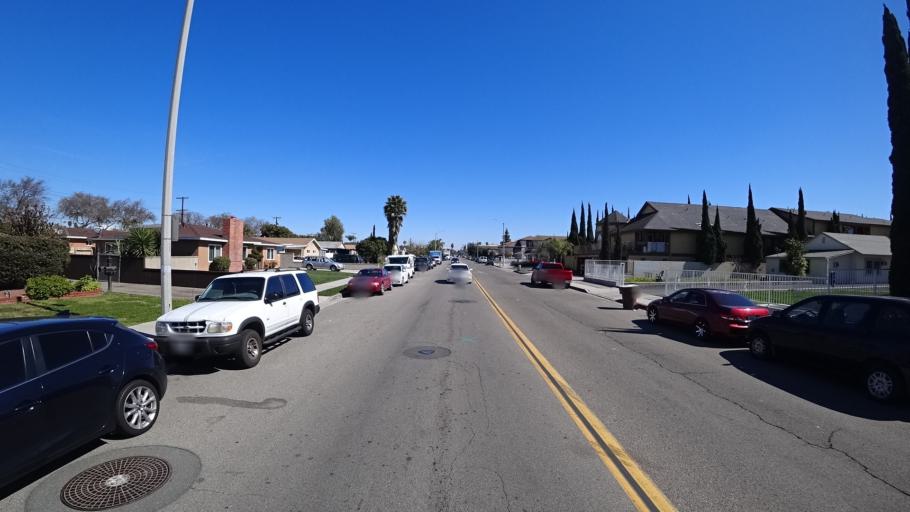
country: US
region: California
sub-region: Orange County
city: Anaheim
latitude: 33.8221
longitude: -117.9143
